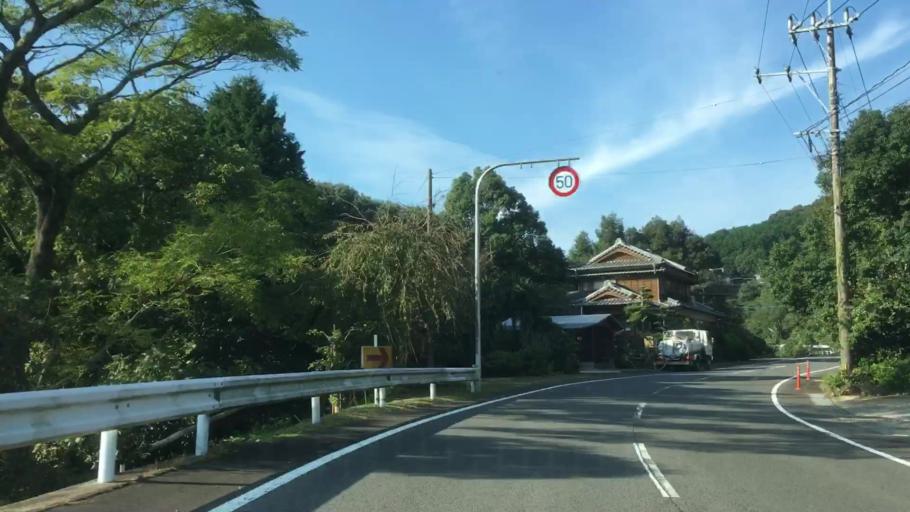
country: JP
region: Nagasaki
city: Sasebo
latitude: 32.9823
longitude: 129.7176
